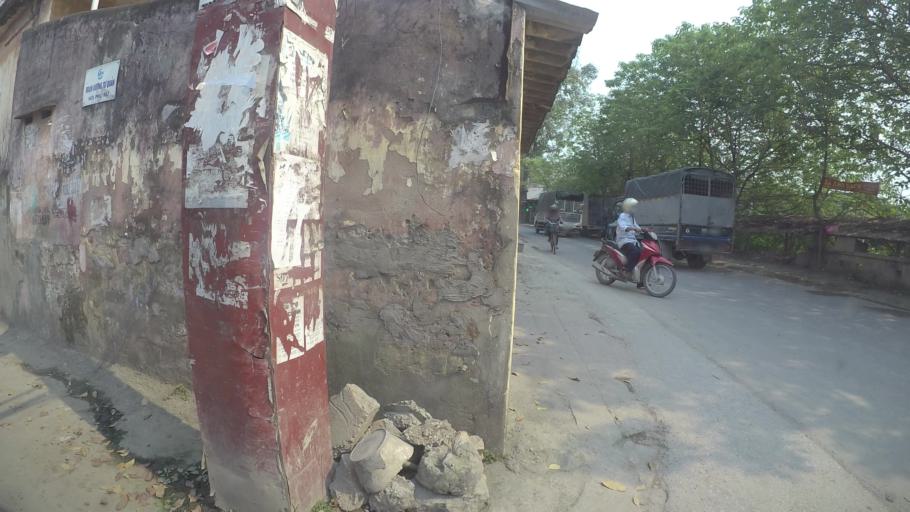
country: VN
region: Ha Noi
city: Ha Dong
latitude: 20.9979
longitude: 105.7519
